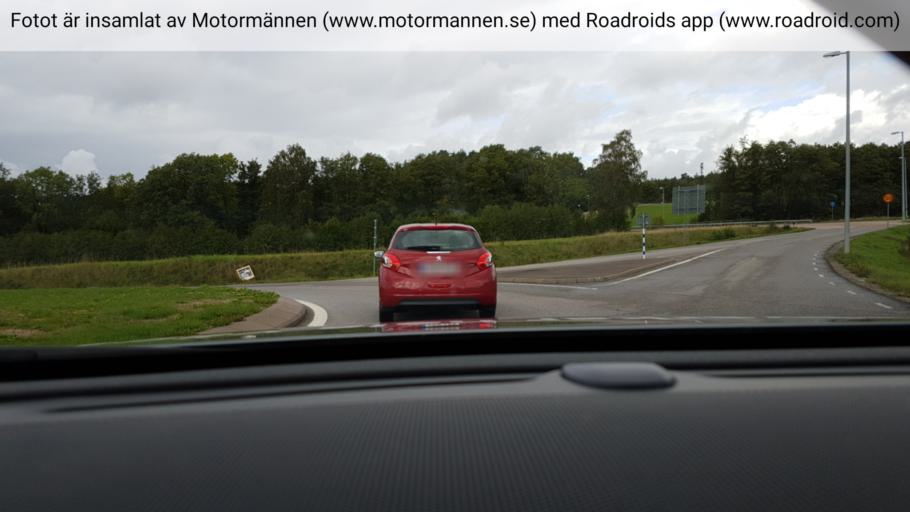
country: SE
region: Vaestra Goetaland
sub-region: Stenungsunds Kommun
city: Stenungsund
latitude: 58.0694
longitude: 11.8563
